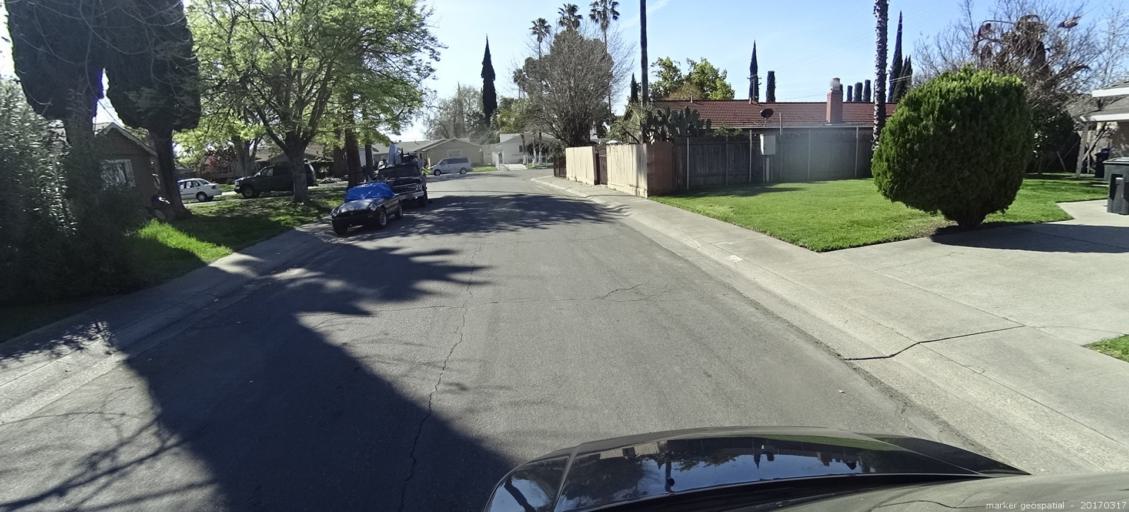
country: US
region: California
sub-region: Sacramento County
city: Parkway
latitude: 38.4897
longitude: -121.4911
